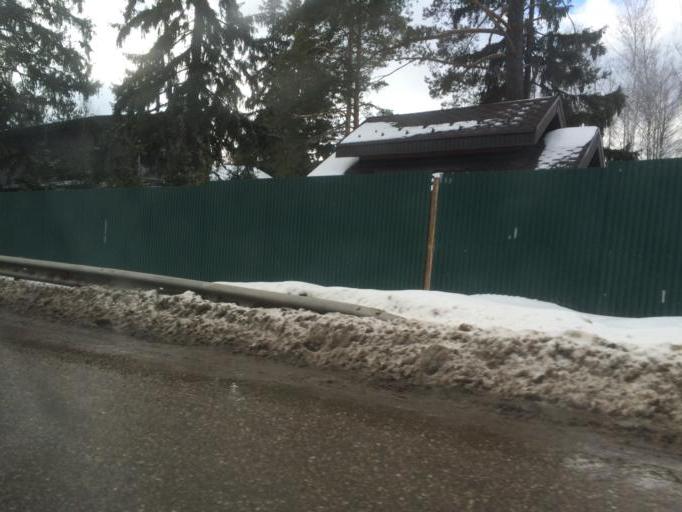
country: RU
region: Moskovskaya
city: Pavlovskaya Sloboda
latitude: 55.8042
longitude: 37.1269
